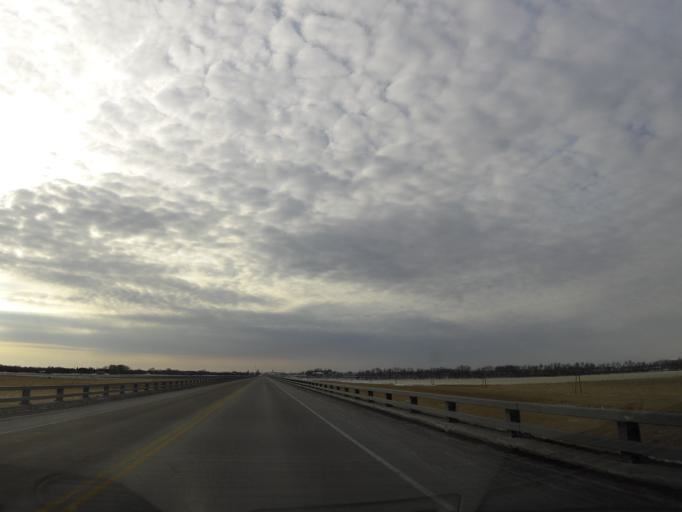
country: US
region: Minnesota
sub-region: Kittson County
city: Hallock
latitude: 48.5722
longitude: -97.1528
